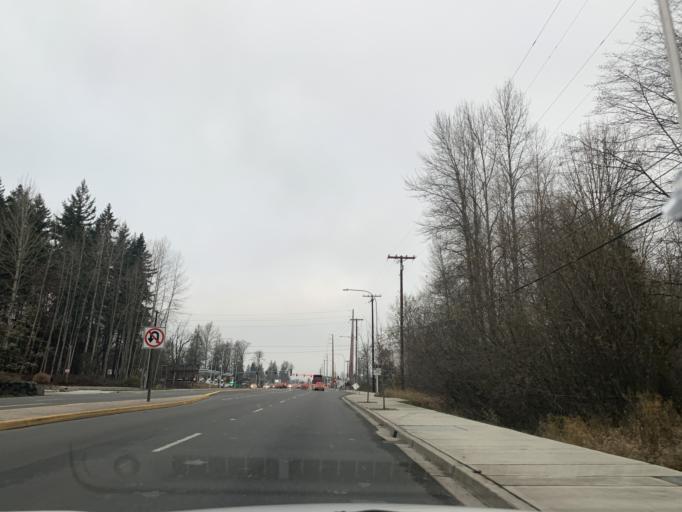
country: US
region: Washington
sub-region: Pierce County
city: Fife Heights
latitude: 47.2807
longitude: -122.3230
